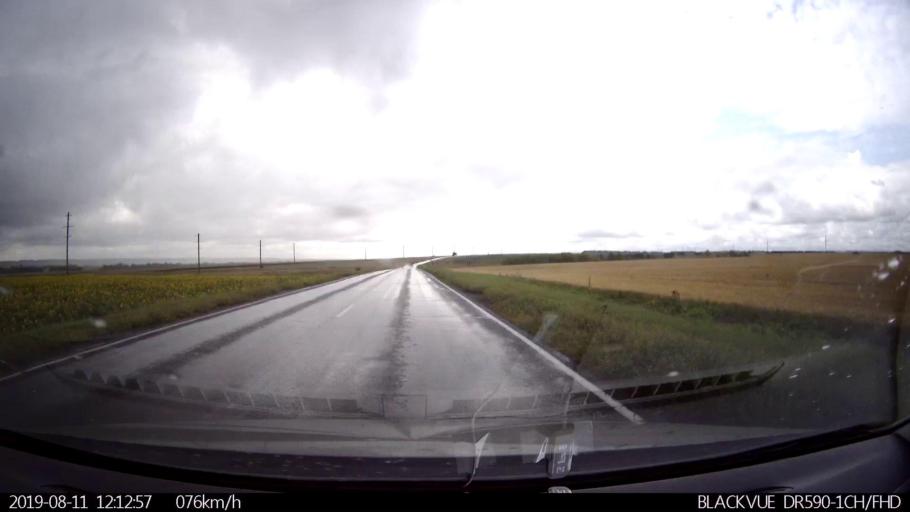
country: RU
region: Ulyanovsk
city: Silikatnyy
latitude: 53.9670
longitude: 47.9945
